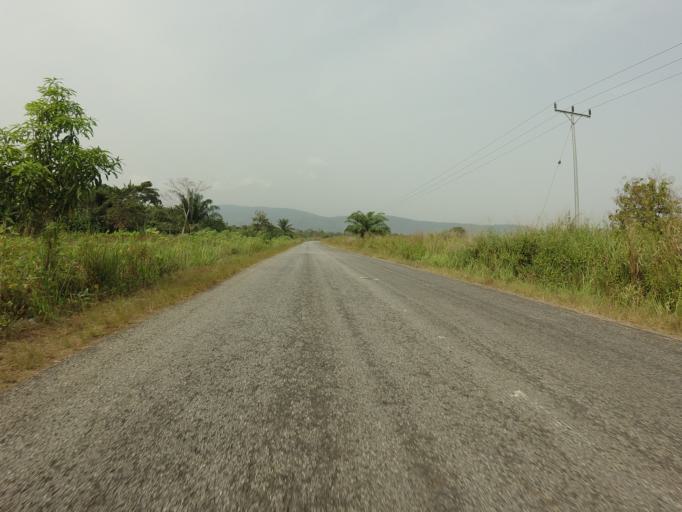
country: GH
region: Volta
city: Ho
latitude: 6.5737
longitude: 0.3454
